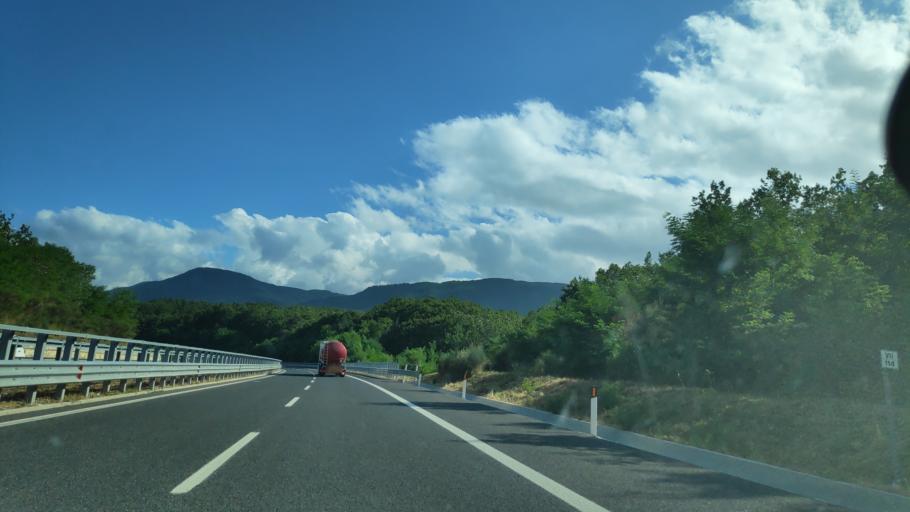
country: IT
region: Campania
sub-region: Provincia di Salerno
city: Casalbuono
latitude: 40.2415
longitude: 15.6596
